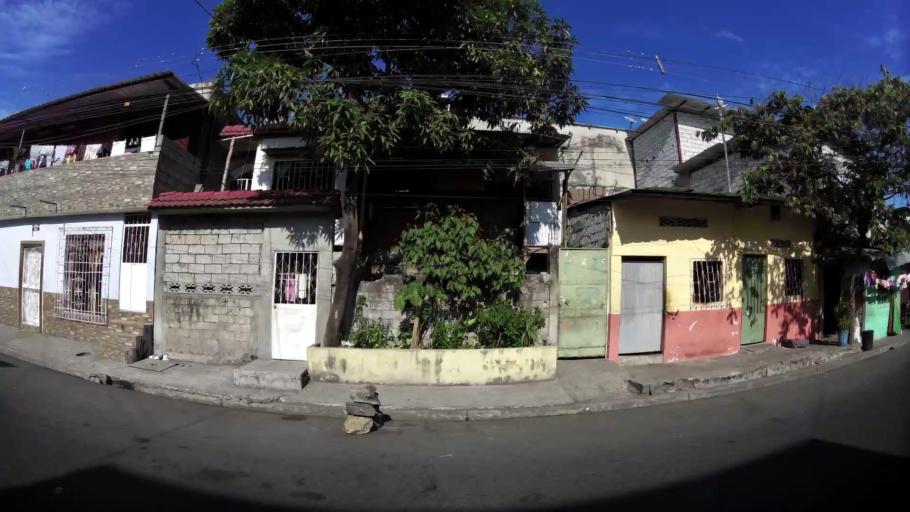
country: EC
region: Guayas
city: Guayaquil
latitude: -2.2187
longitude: -79.9288
